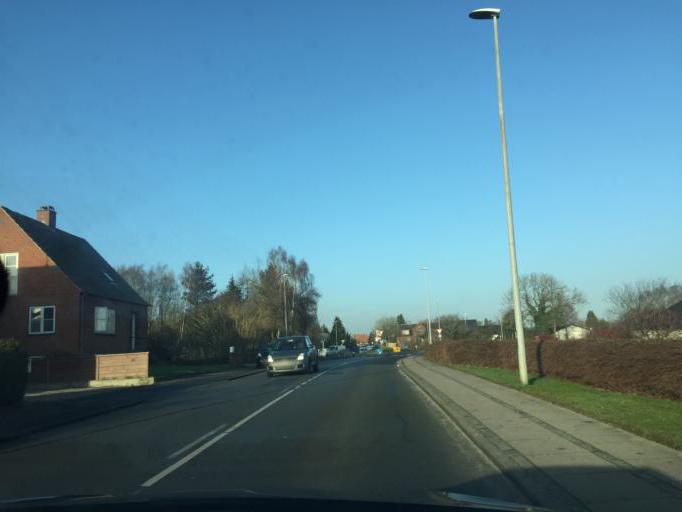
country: DK
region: South Denmark
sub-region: Faaborg-Midtfyn Kommune
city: Faaborg
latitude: 55.1077
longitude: 10.2249
